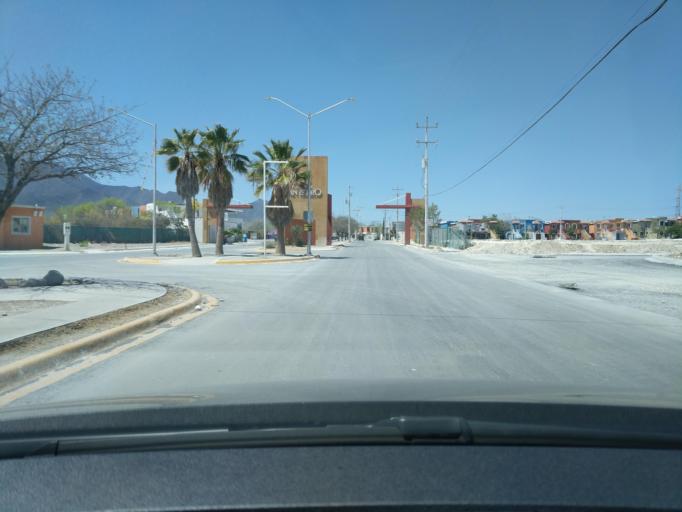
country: MX
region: Nuevo Leon
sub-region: Salinas Victoria
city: Las Torres
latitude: 25.9633
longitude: -100.3049
